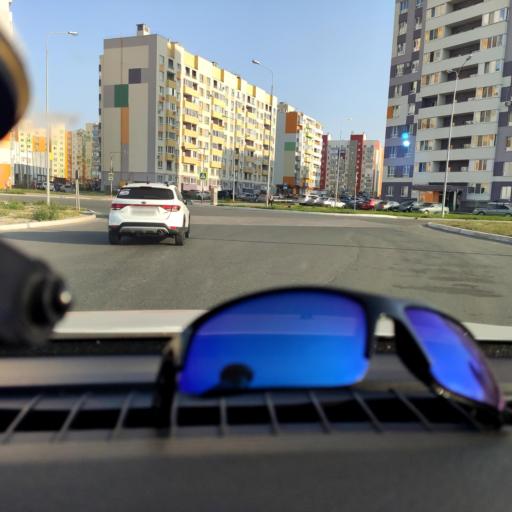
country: RU
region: Samara
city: Samara
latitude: 53.0953
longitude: 50.1593
